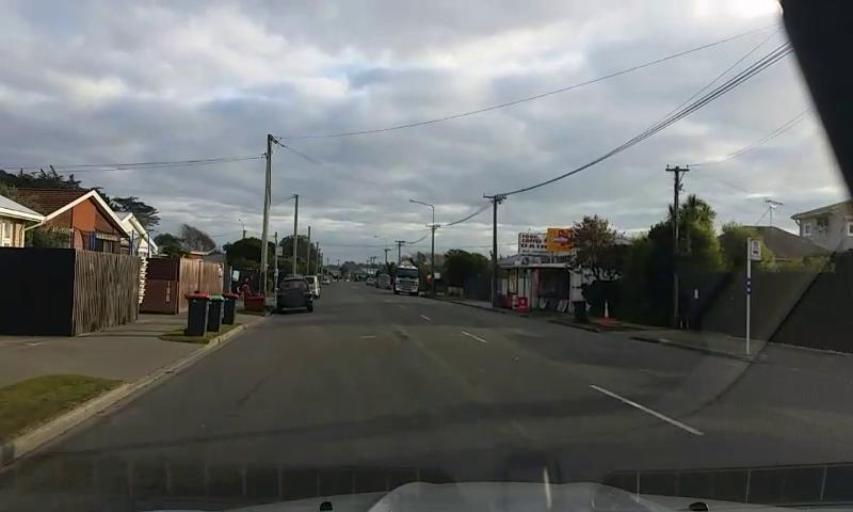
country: NZ
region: Canterbury
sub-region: Christchurch City
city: Christchurch
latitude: -43.5185
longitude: 172.7308
